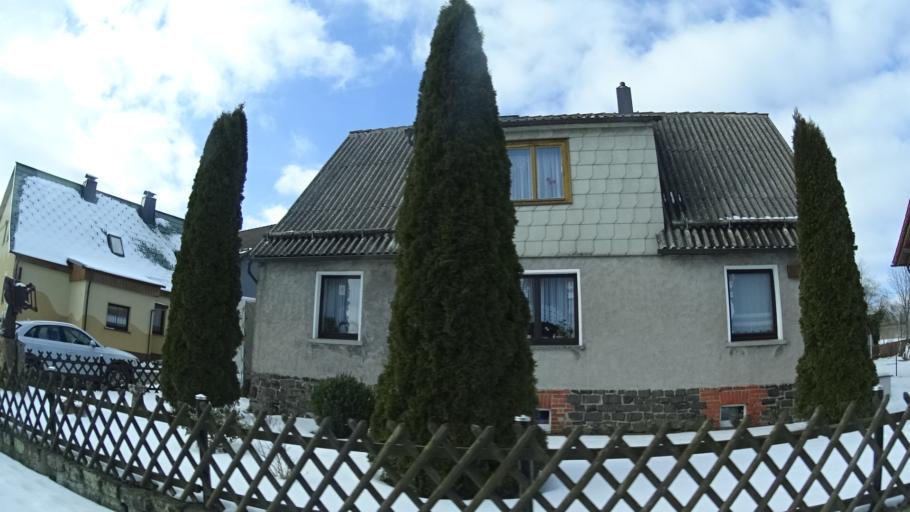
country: DE
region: Thuringia
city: Birx
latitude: 50.5310
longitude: 10.0472
